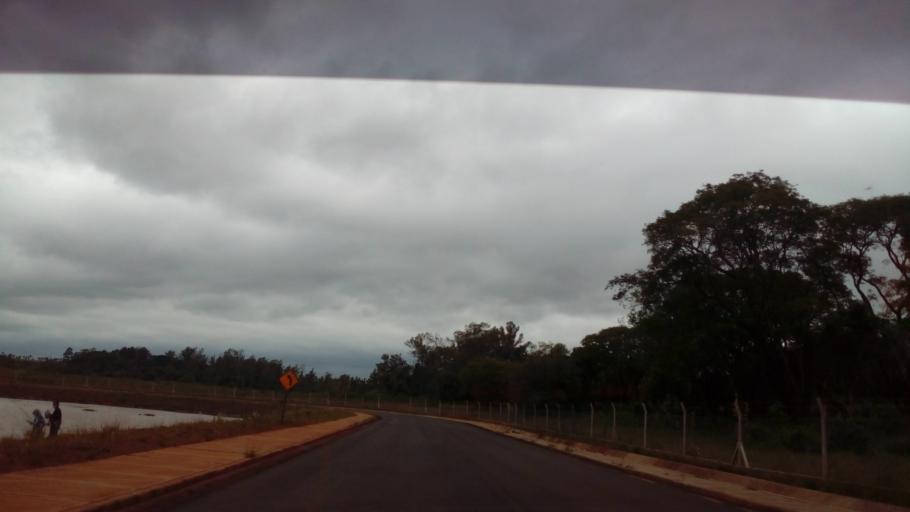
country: AR
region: Misiones
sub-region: Departamento de Candelaria
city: Candelaria
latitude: -27.4519
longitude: -55.7745
